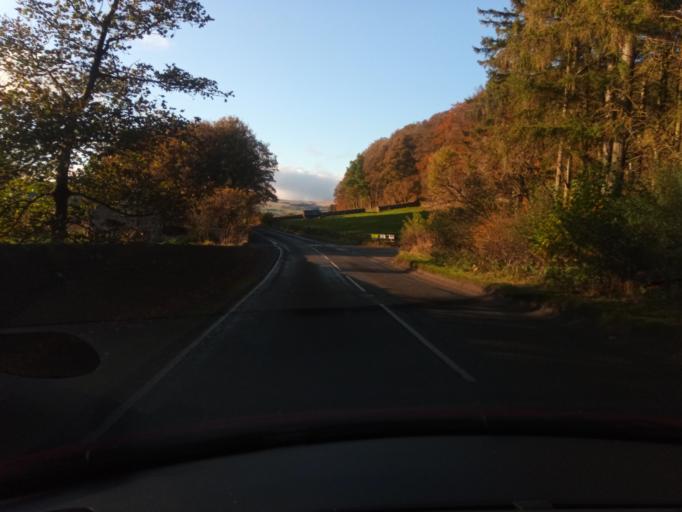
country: GB
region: England
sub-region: County Durham
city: Stanhope
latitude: 54.7331
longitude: -1.9781
